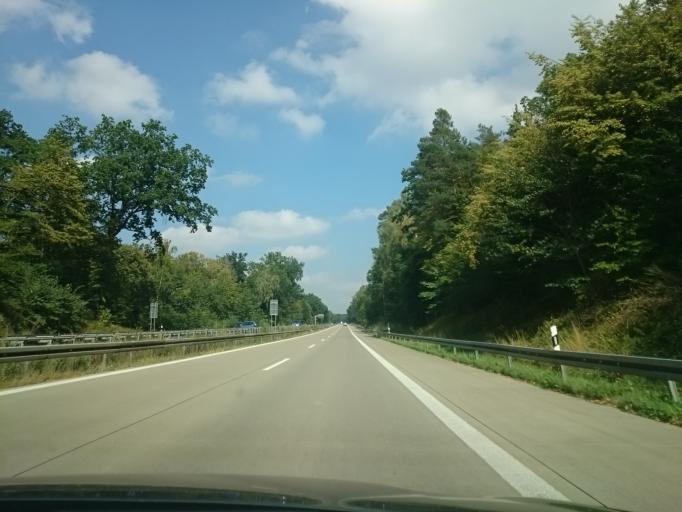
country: DE
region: Brandenburg
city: Gerswalde
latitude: 53.1332
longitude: 13.8854
